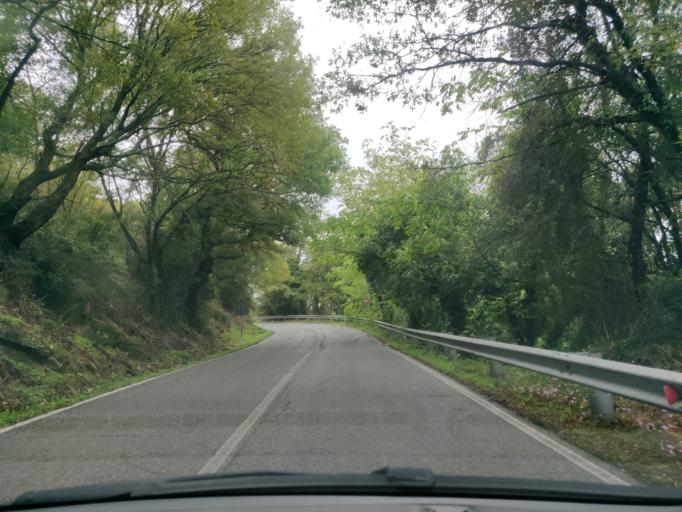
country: IT
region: Latium
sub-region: Citta metropolitana di Roma Capitale
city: Allumiere
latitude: 42.1446
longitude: 11.8824
